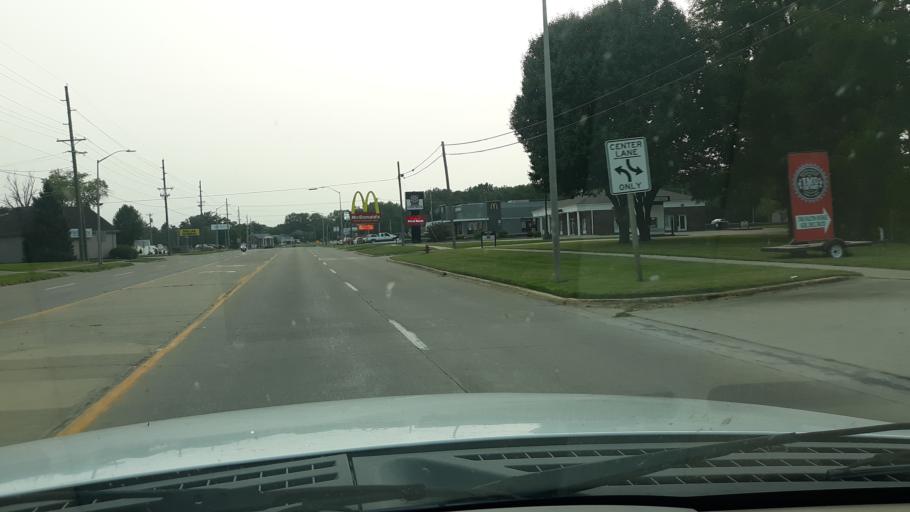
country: US
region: Illinois
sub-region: White County
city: Carmi
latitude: 38.0801
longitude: -88.1764
